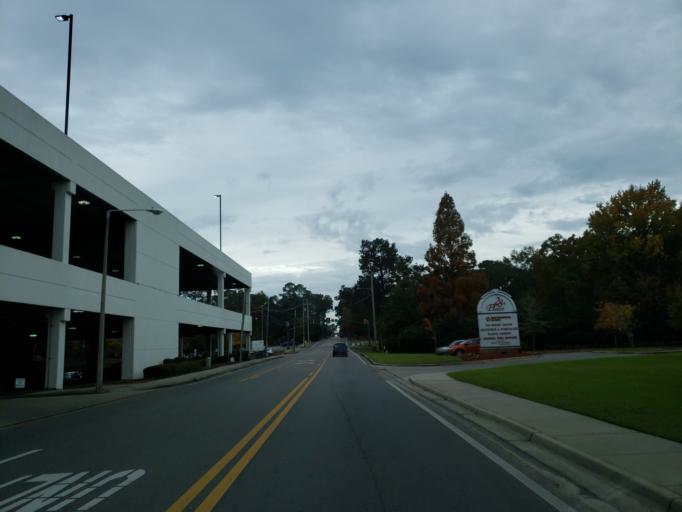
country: US
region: Mississippi
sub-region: Forrest County
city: Hattiesburg
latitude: 31.3182
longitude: -89.3313
